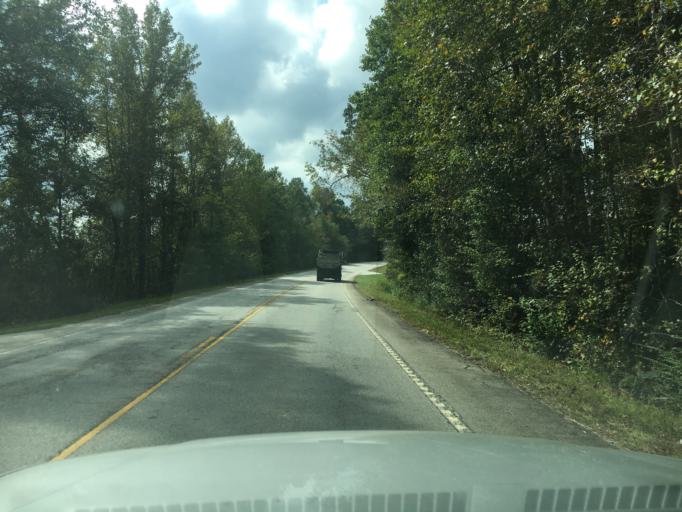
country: US
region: South Carolina
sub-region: Greenville County
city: Tigerville
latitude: 35.0477
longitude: -82.2614
